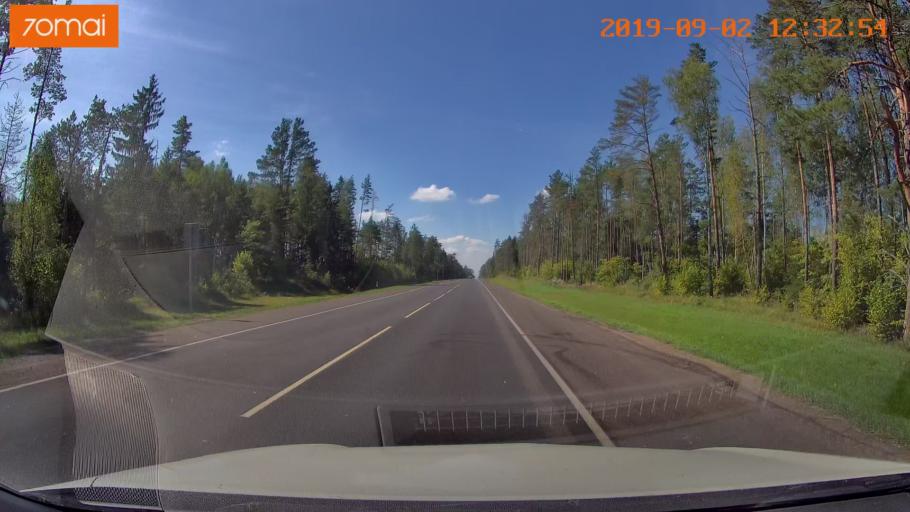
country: RU
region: Smolensk
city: Shumyachi
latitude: 53.8215
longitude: 32.4402
